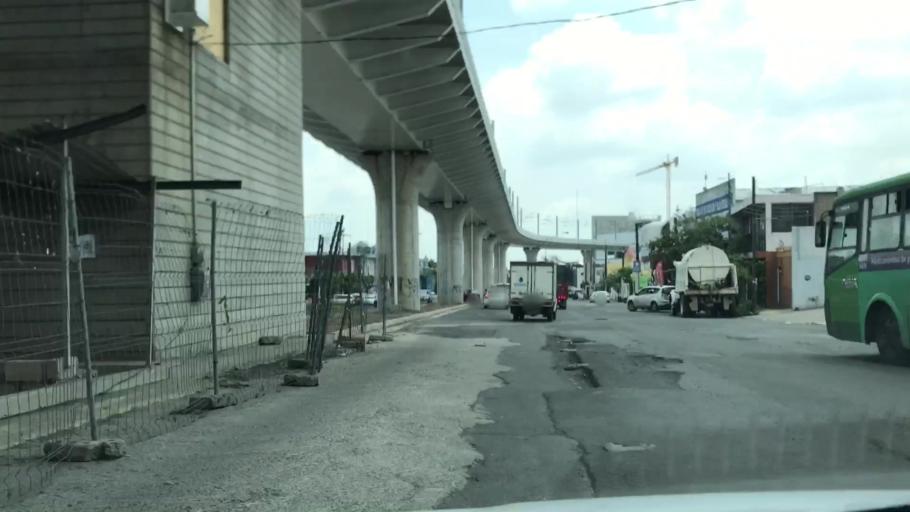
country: MX
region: Jalisco
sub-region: Zapopan
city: Zapopan
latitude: 20.7287
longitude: -103.3890
